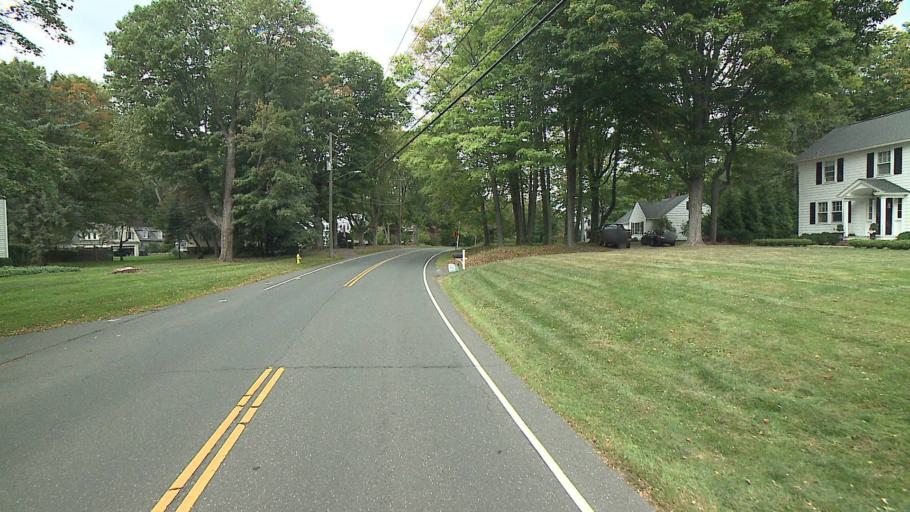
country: US
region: Connecticut
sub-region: Fairfield County
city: Ridgefield
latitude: 41.2653
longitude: -73.4961
